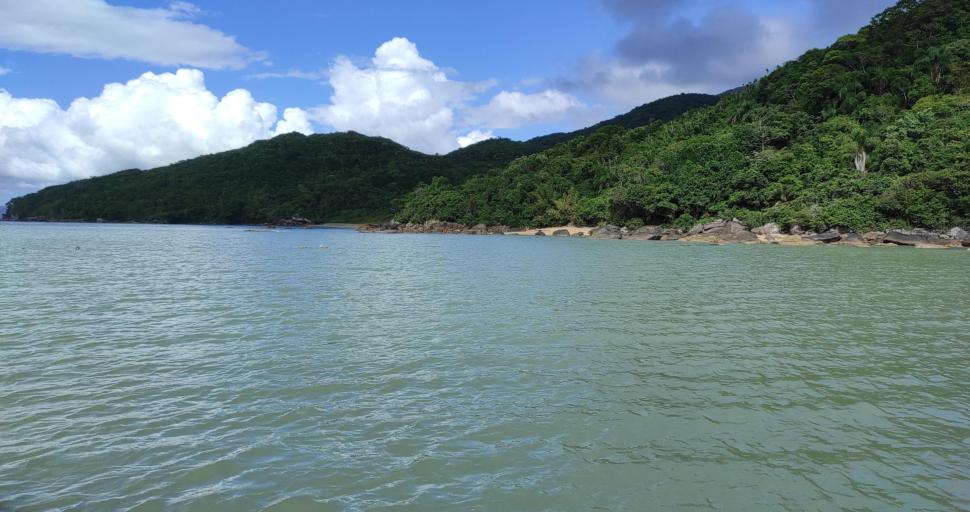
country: BR
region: Santa Catarina
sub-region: Porto Belo
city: Porto Belo
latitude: -27.1880
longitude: -48.5472
